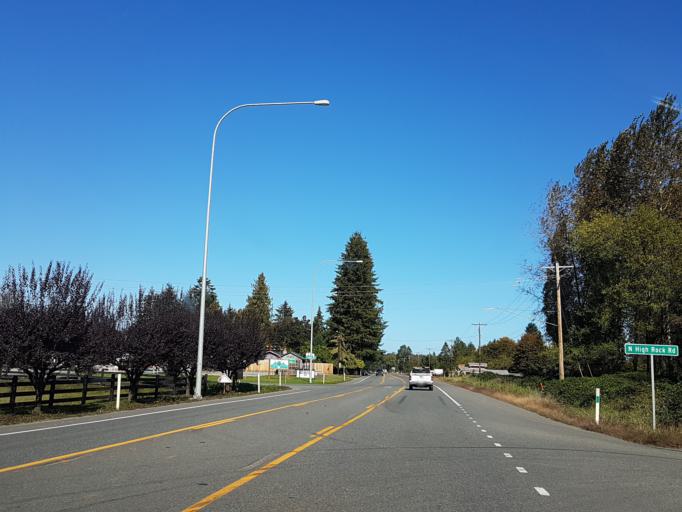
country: US
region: Washington
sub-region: Snohomish County
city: Monroe
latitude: 47.8331
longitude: -121.9695
